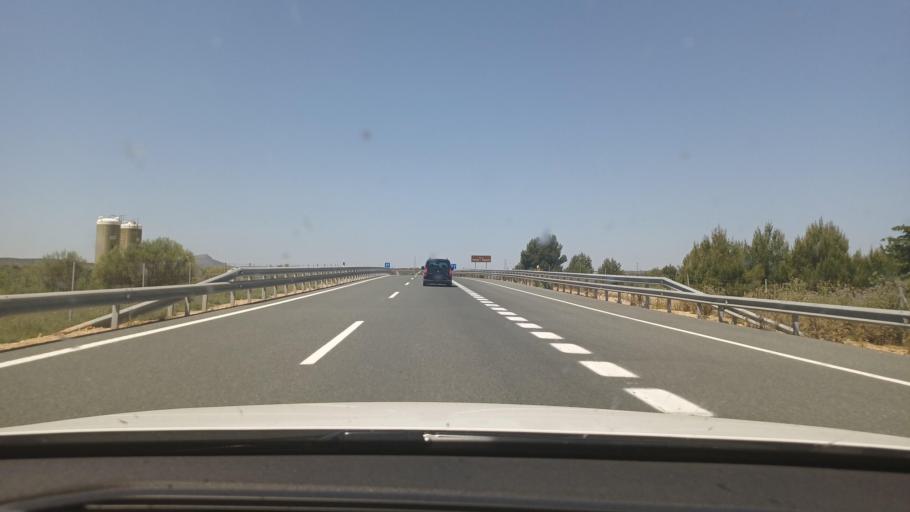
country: ES
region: Castille-La Mancha
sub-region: Provincia de Albacete
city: Alpera
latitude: 38.8784
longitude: -1.2257
